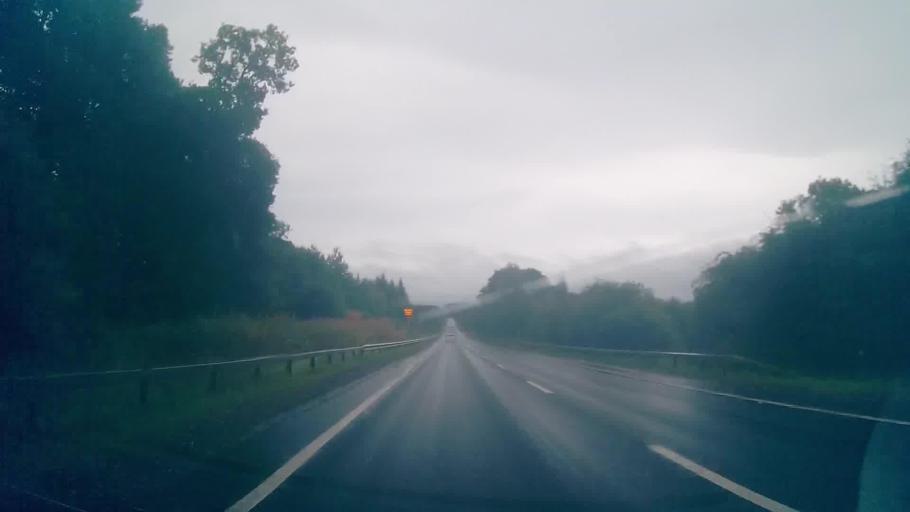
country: GB
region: Scotland
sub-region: East Ayrshire
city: Auchinleck
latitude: 55.4608
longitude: -4.2945
